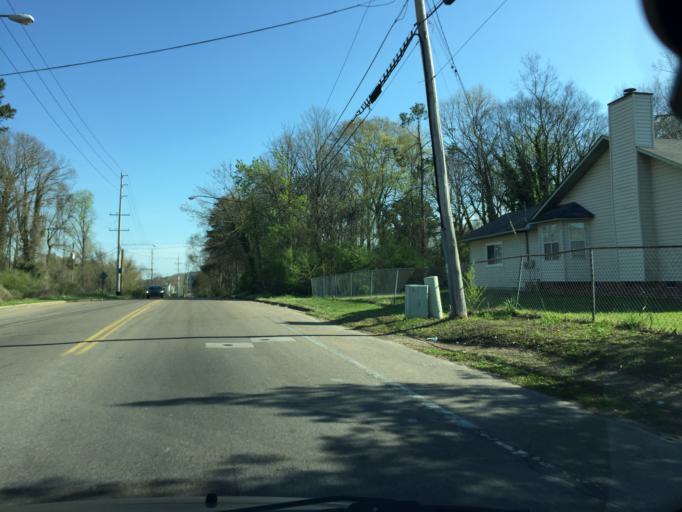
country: US
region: Tennessee
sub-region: Hamilton County
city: East Ridge
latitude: 35.0315
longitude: -85.2424
